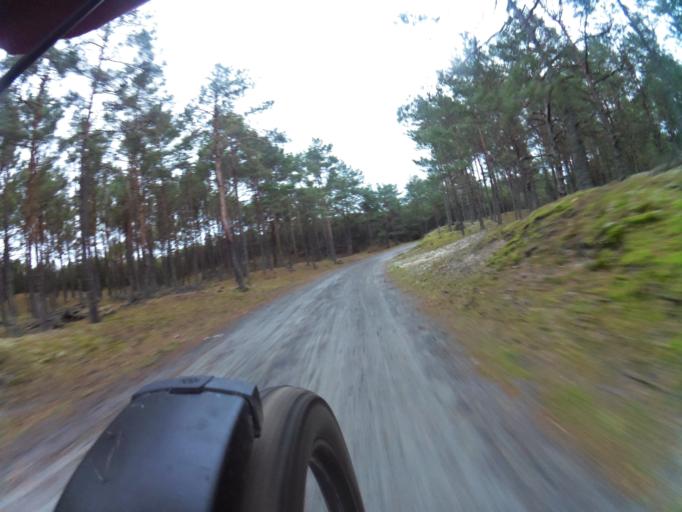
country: PL
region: Pomeranian Voivodeship
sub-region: Powiat wejherowski
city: Choczewo
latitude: 54.7878
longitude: 17.7476
